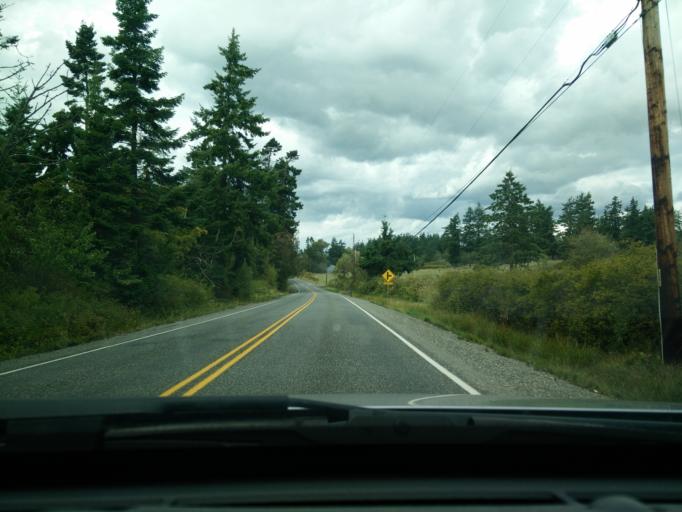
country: US
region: Washington
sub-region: Skagit County
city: Anacortes
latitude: 48.4993
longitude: -122.4817
